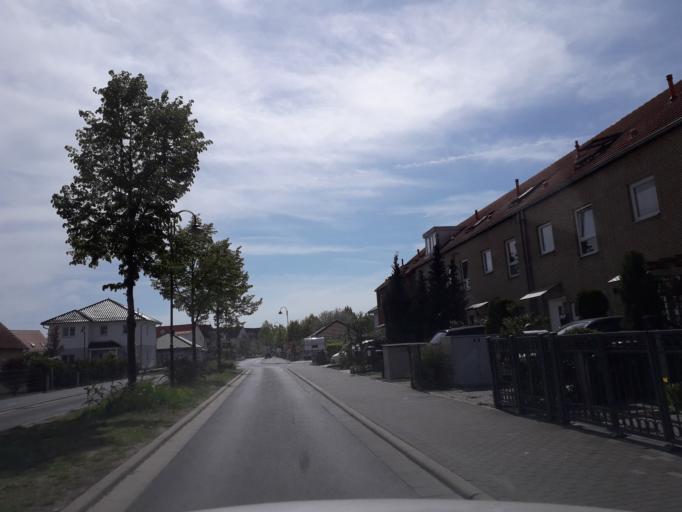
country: DE
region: Brandenburg
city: Wustermark
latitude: 52.5438
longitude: 12.9360
